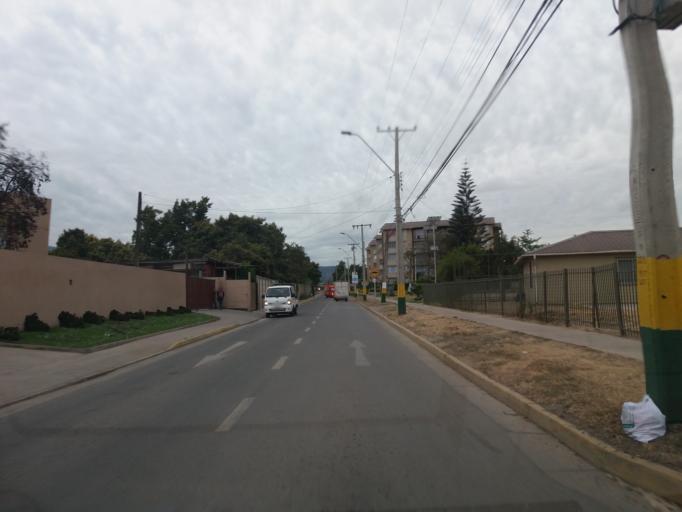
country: CL
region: Valparaiso
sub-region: Provincia de Quillota
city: Quillota
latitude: -32.8447
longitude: -71.2272
